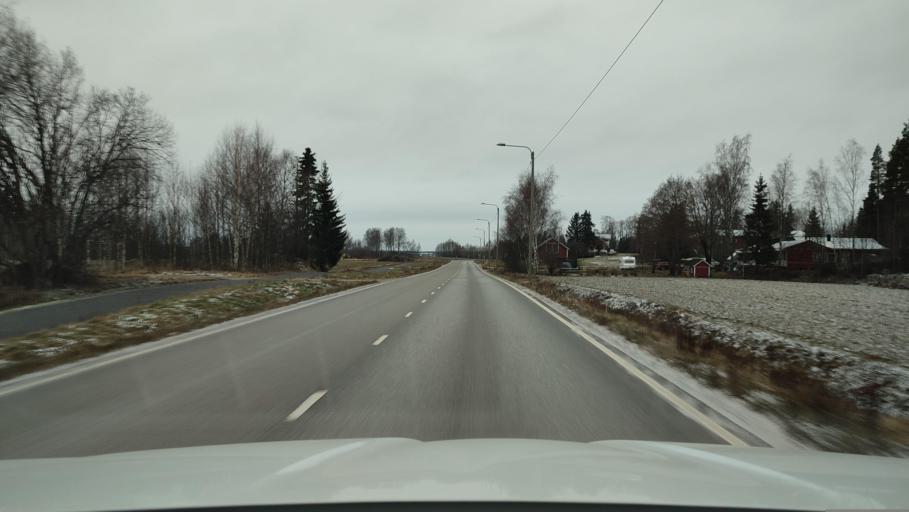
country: FI
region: Ostrobothnia
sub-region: Vaasa
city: Ristinummi
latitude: 63.0345
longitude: 21.7894
